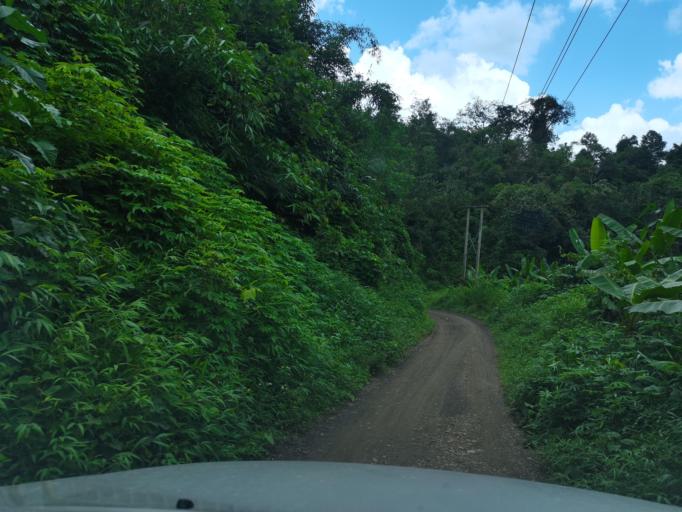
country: LA
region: Loungnamtha
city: Muang Long
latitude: 20.7674
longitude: 101.0177
